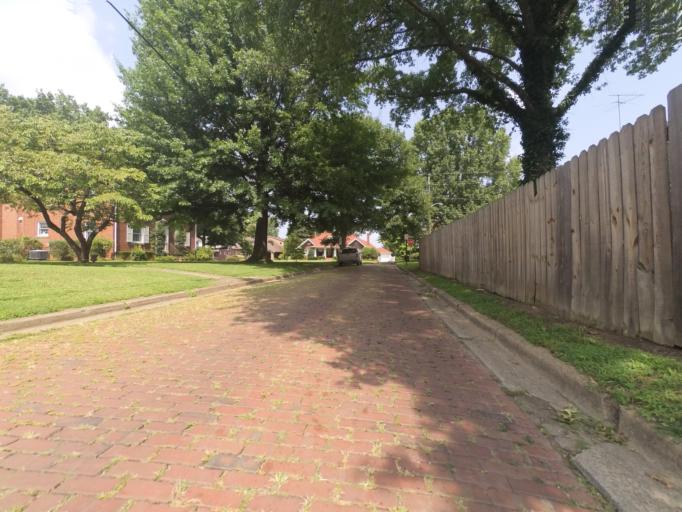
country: US
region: West Virginia
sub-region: Cabell County
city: Huntington
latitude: 38.4329
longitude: -82.3990
